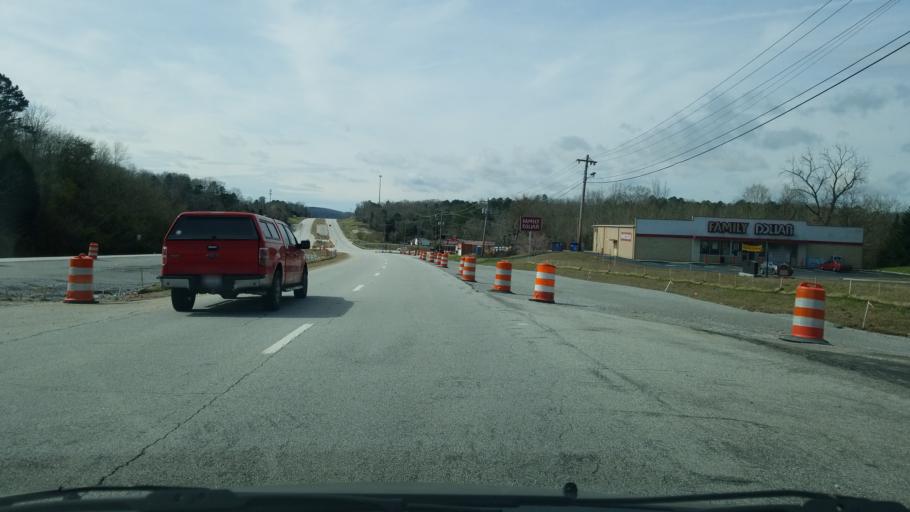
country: US
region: Tennessee
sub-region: Hamilton County
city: Lakesite
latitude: 35.1825
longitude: -85.0660
